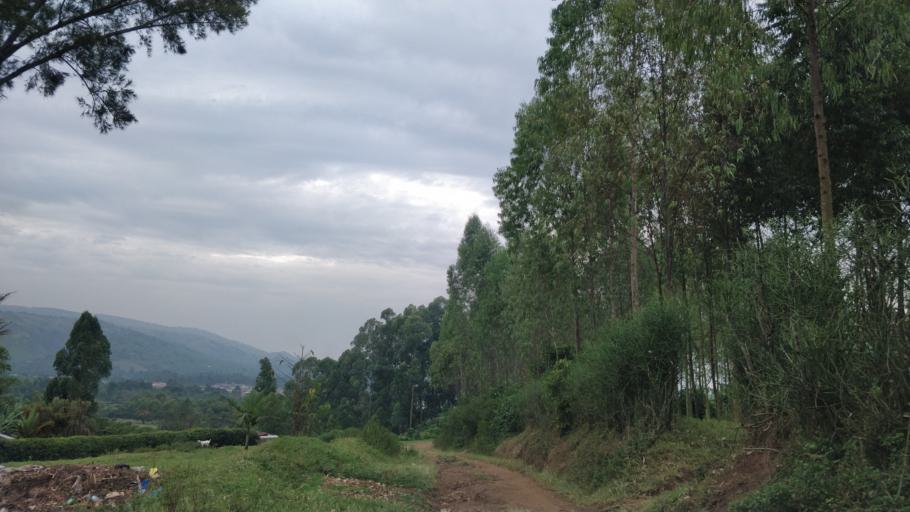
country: UG
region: Western Region
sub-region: Sheema District
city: Kibingo
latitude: -0.7006
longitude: 30.3934
